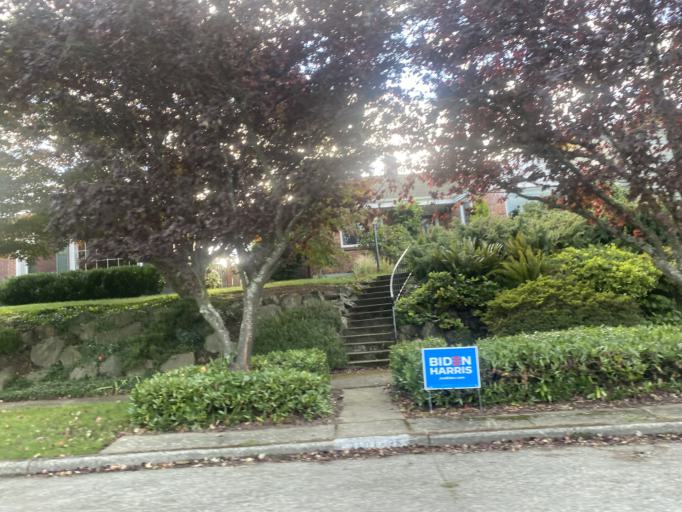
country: US
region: Washington
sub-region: King County
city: Seattle
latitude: 47.6379
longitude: -122.4021
